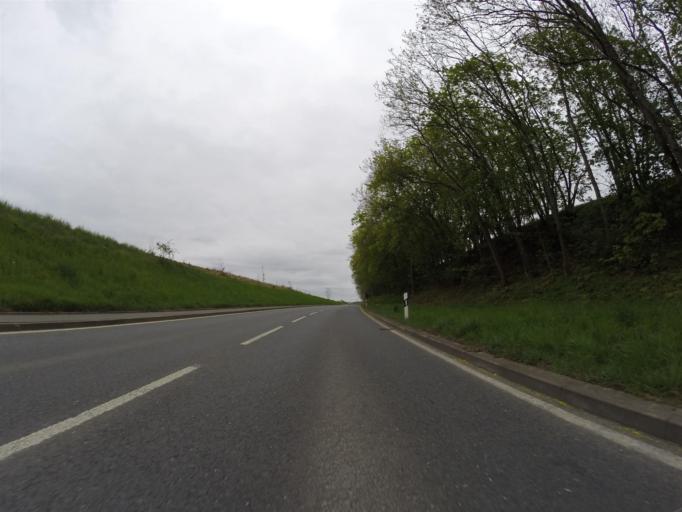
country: DE
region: Thuringia
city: Camburg
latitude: 51.0586
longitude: 11.7129
